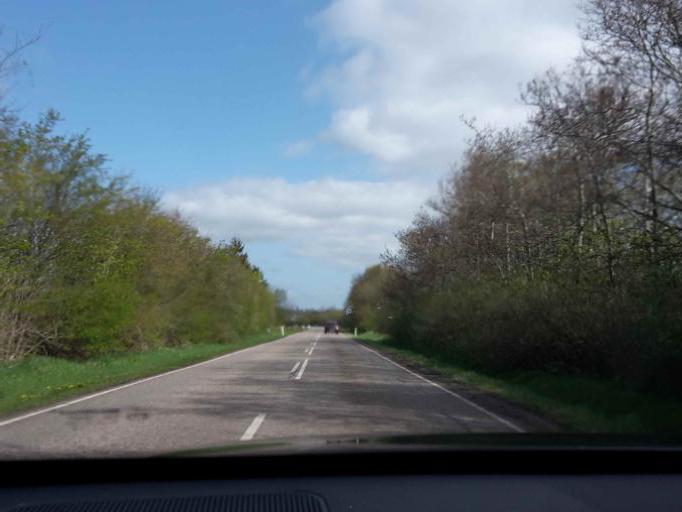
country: DK
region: South Denmark
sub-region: Varde Kommune
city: Olgod
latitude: 55.7805
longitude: 8.7054
